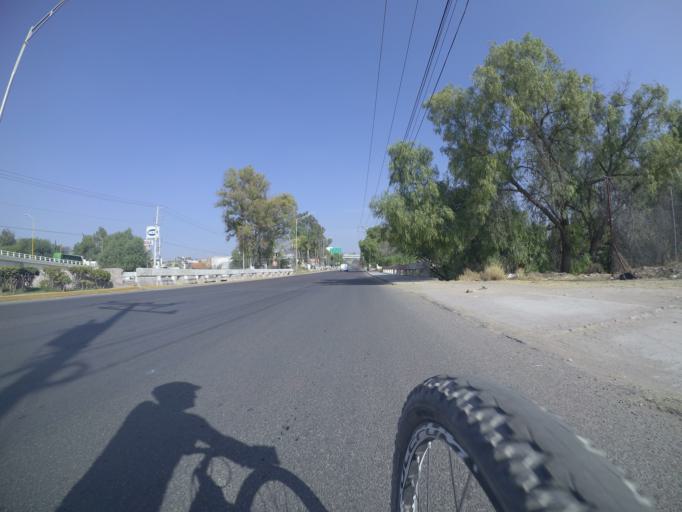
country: MX
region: Aguascalientes
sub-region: Jesus Maria
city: Corral de Barrancos
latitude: 21.9530
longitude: -102.3356
